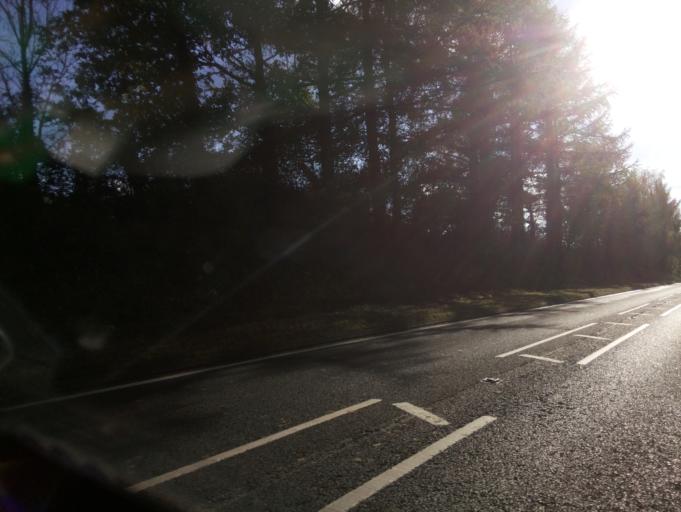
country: GB
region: Wales
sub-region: Sir Powys
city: Brecon
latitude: 51.9175
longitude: -3.4669
